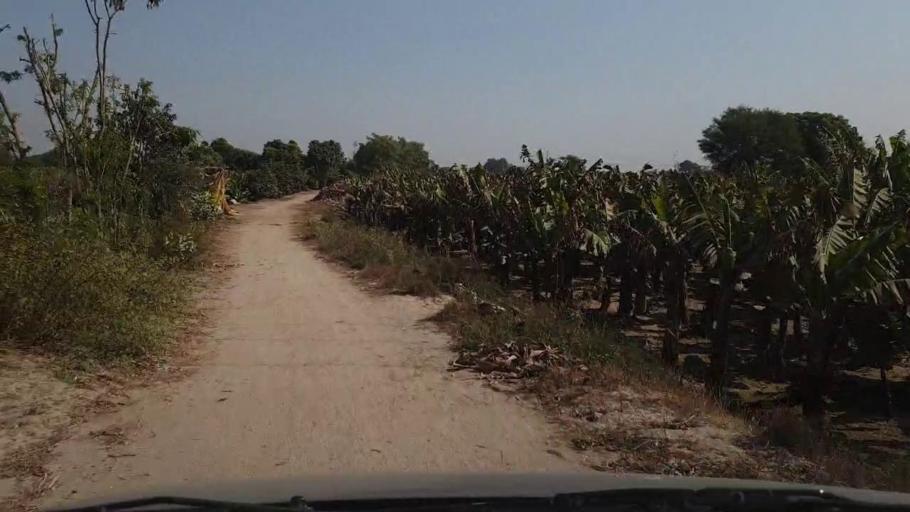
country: PK
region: Sindh
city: Tando Allahyar
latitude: 25.4342
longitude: 68.6455
